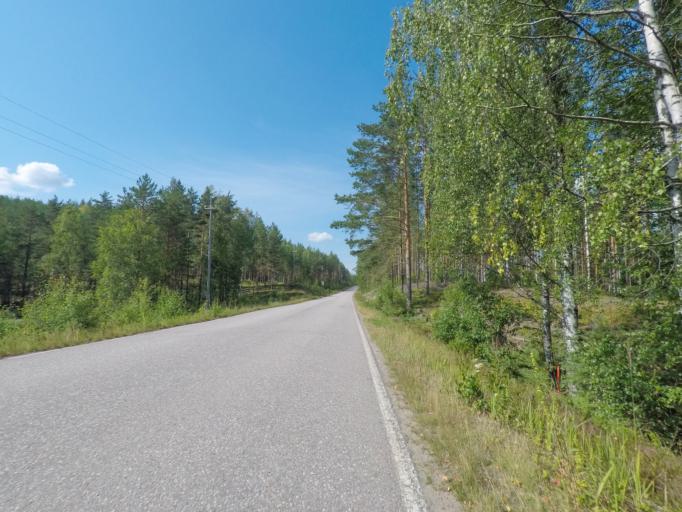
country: FI
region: Southern Savonia
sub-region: Mikkeli
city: Puumala
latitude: 61.4623
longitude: 28.1741
